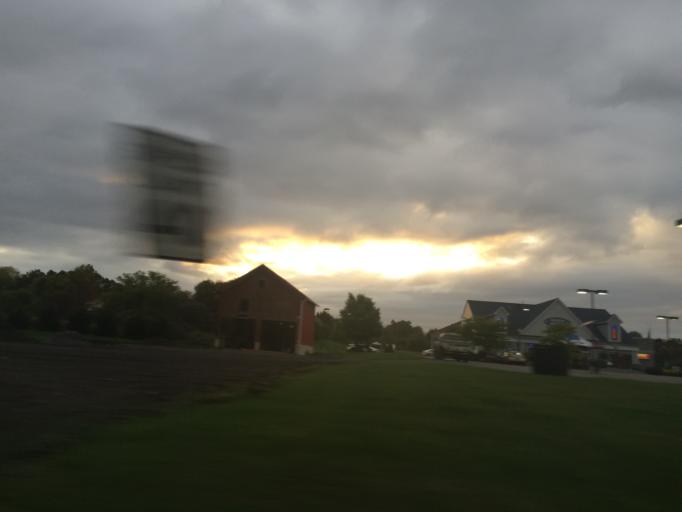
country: US
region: New York
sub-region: Erie County
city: Billington Heights
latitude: 42.7932
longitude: -78.6215
